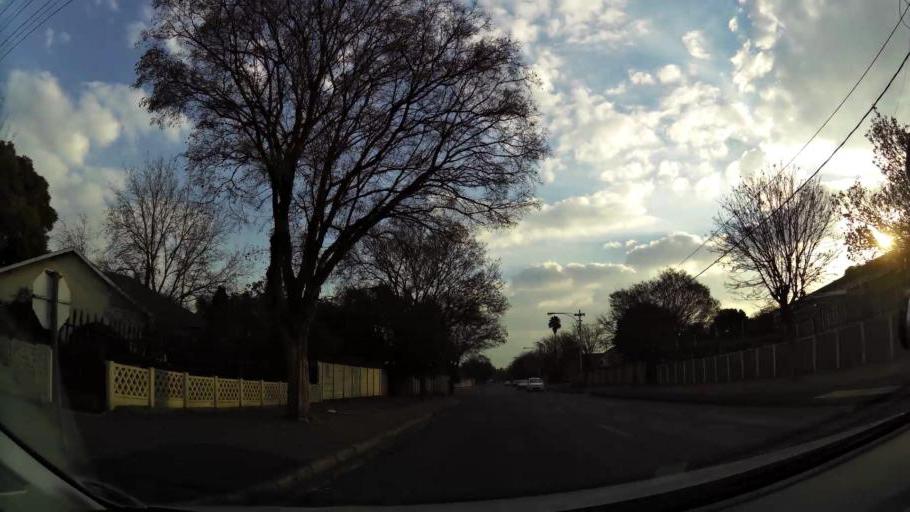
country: ZA
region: Gauteng
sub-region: Ekurhuleni Metropolitan Municipality
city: Germiston
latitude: -26.1819
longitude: 28.1733
